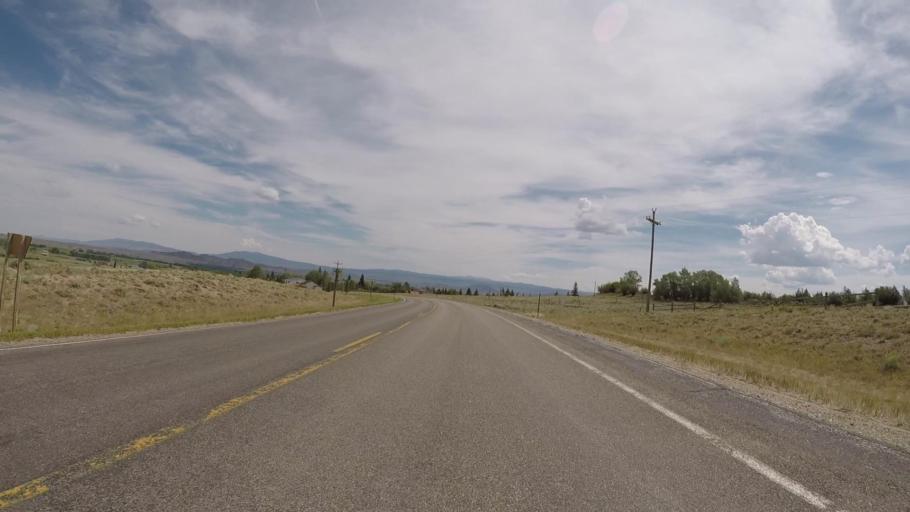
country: US
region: Wyoming
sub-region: Carbon County
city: Saratoga
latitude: 41.2040
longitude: -106.8004
